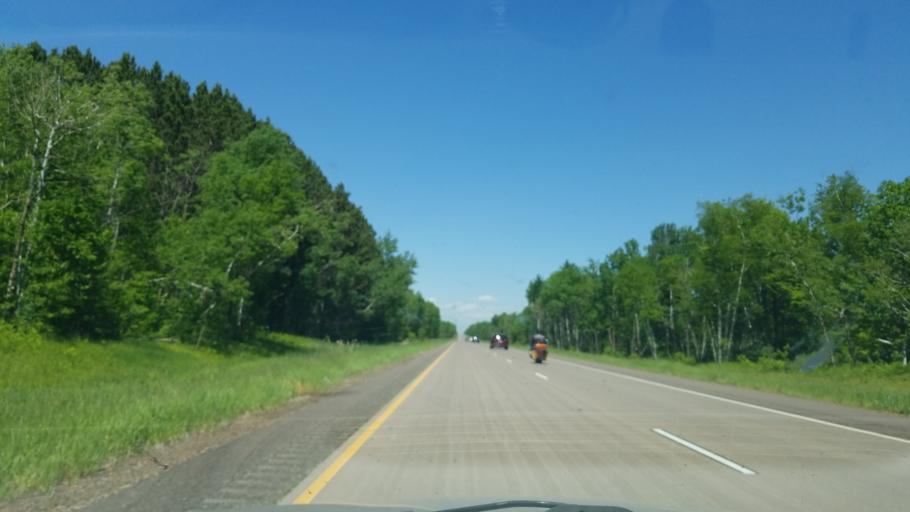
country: US
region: Minnesota
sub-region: Pine County
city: Hinckley
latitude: 46.0583
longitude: -92.9102
